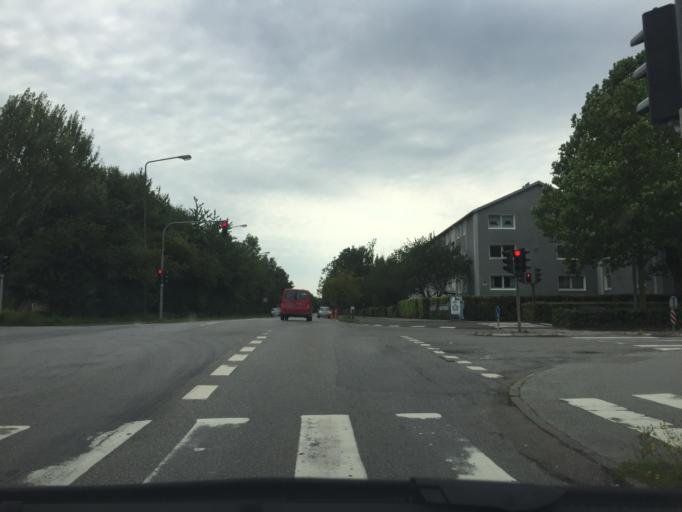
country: DK
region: Capital Region
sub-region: Lyngby-Tarbaek Kommune
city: Kongens Lyngby
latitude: 55.7955
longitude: 12.5296
